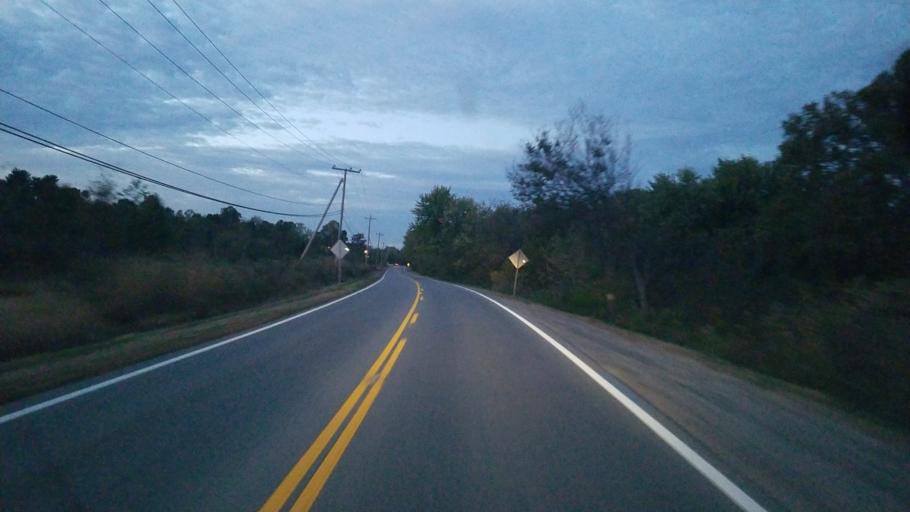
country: US
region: Ohio
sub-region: Scioto County
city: Rosemount
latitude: 38.8045
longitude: -83.0081
